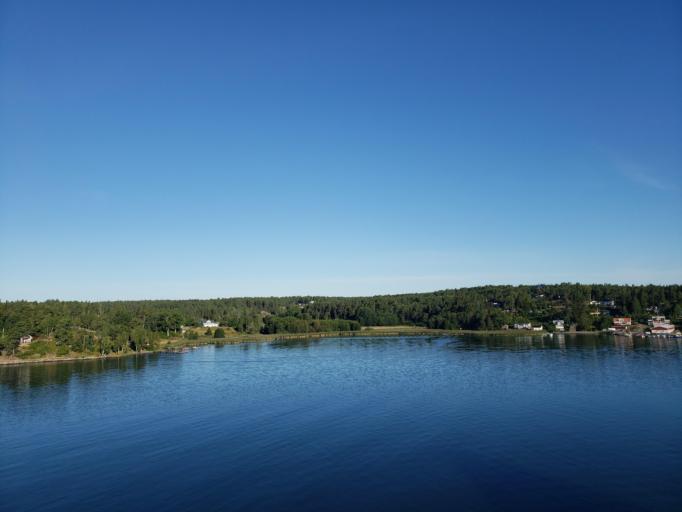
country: SE
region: Stockholm
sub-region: Vaxholms Kommun
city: Vaxholm
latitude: 59.4985
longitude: 18.4666
